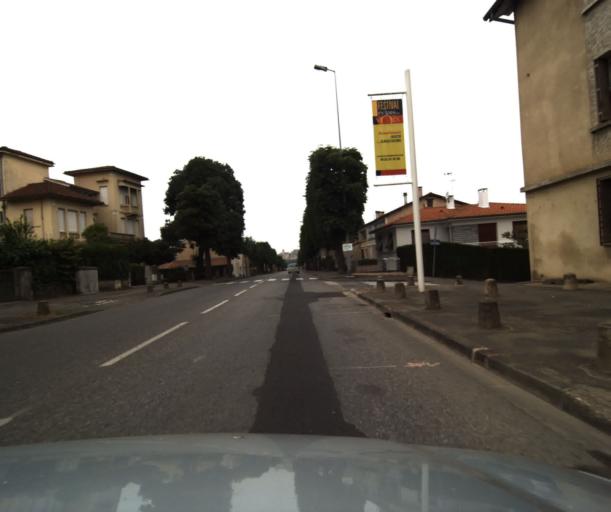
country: FR
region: Midi-Pyrenees
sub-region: Departement du Gers
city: Auch
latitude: 43.6512
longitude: 0.6026
